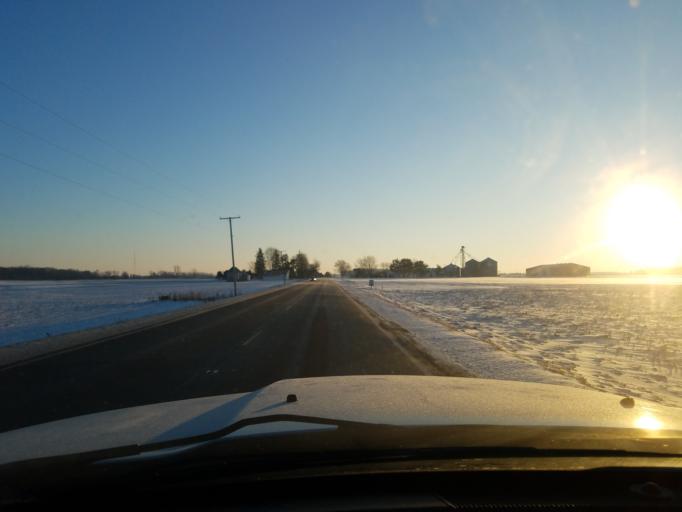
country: US
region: Indiana
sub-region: Marshall County
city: Bremen
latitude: 41.4499
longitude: -86.2246
